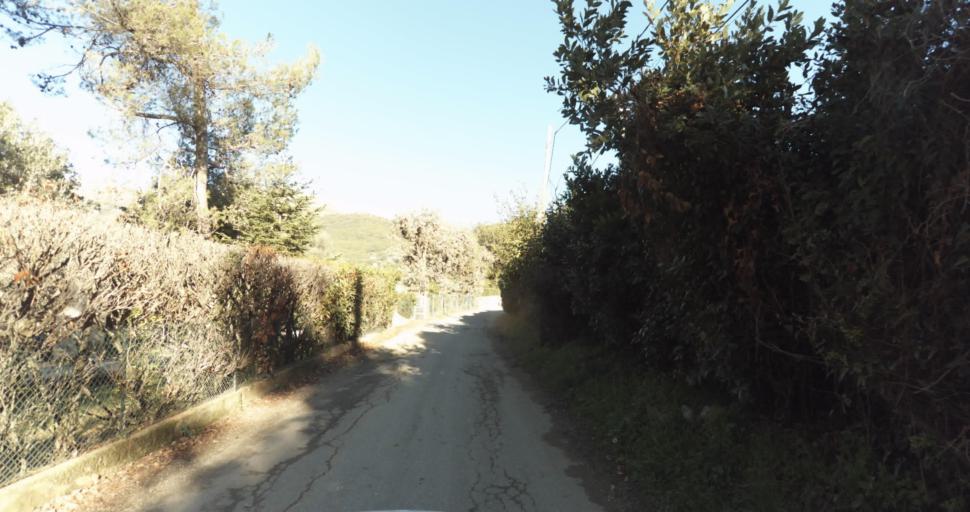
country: FR
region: Provence-Alpes-Cote d'Azur
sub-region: Departement des Alpes-Maritimes
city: Vence
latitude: 43.7140
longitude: 7.0858
